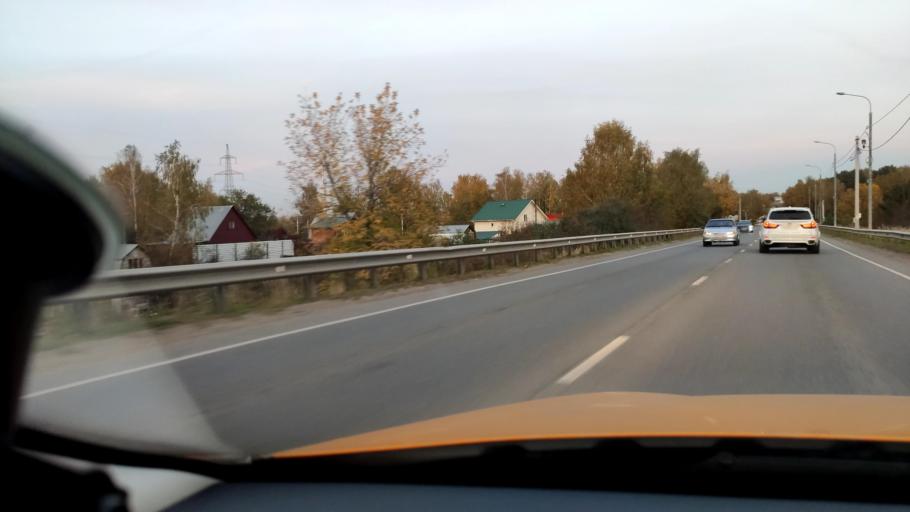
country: RU
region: Moskovskaya
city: Pirogovskiy
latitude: 55.9702
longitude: 37.7035
